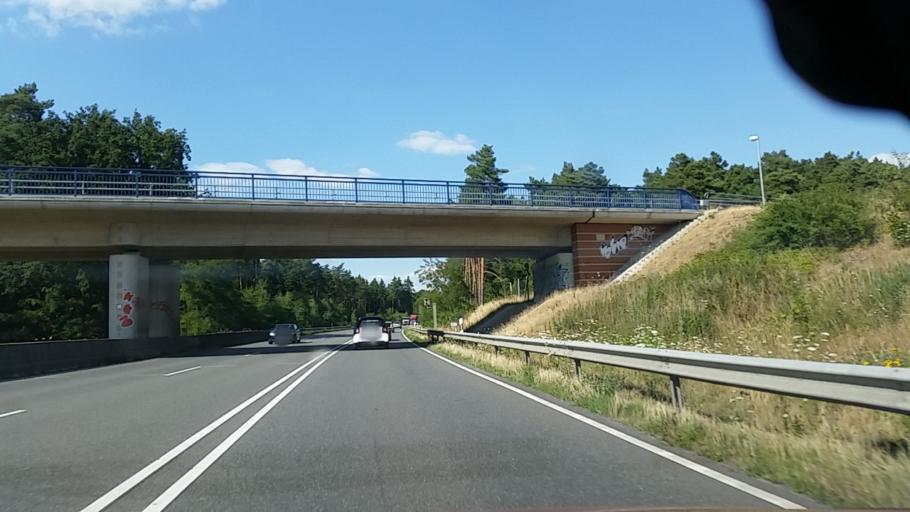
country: DE
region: Lower Saxony
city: Adelheidsdorf
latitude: 52.5525
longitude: 10.0682
